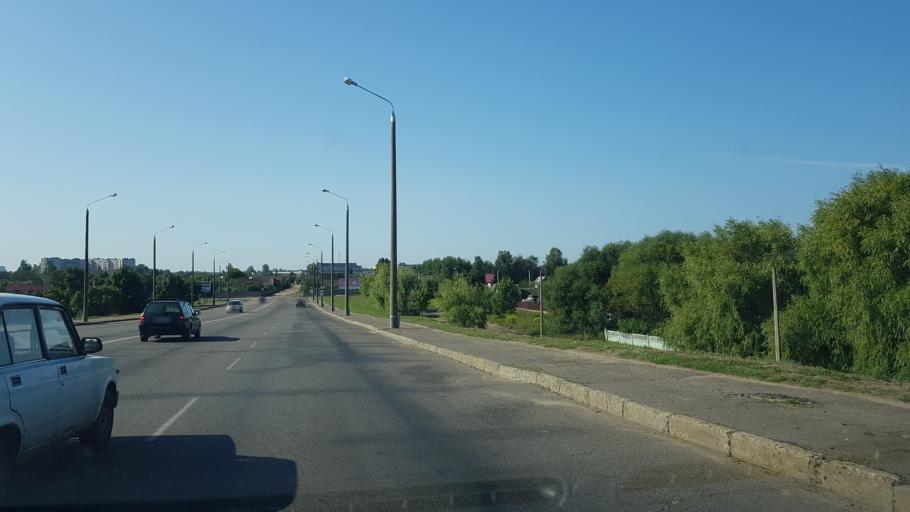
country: BY
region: Mogilev
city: Babruysk
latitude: 53.1374
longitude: 29.1895
